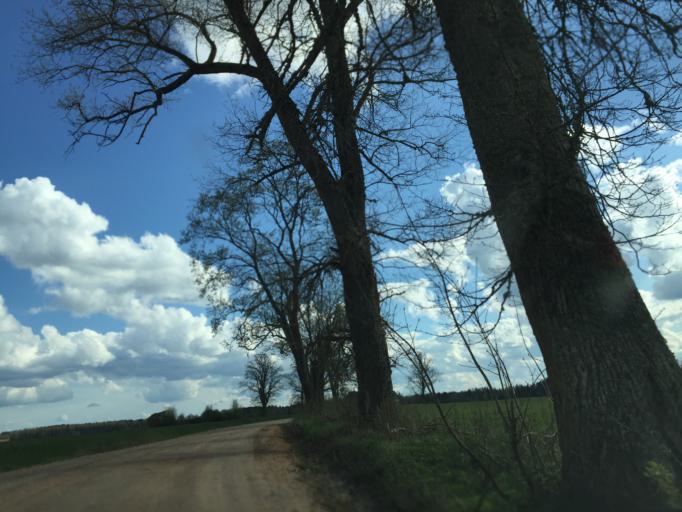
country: LV
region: Beverina
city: Murmuiza
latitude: 57.4410
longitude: 25.5451
